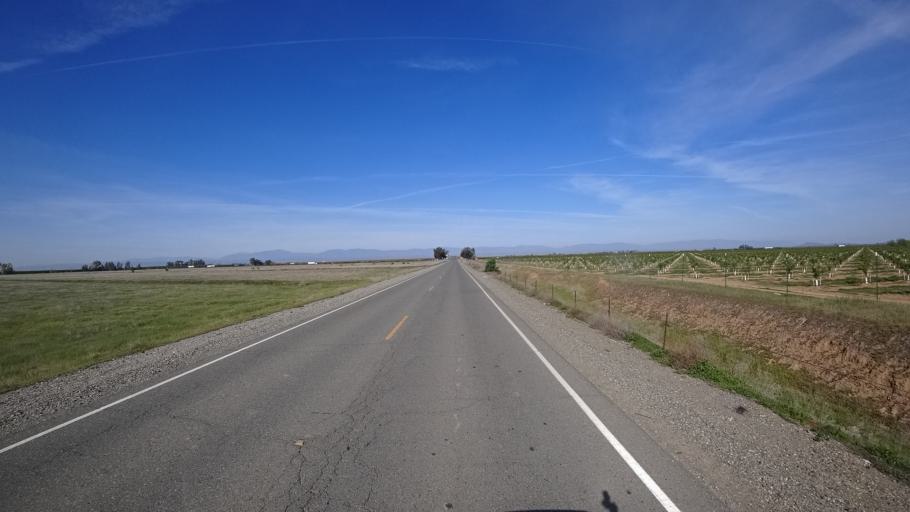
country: US
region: California
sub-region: Glenn County
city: Willows
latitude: 39.6244
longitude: -122.1981
